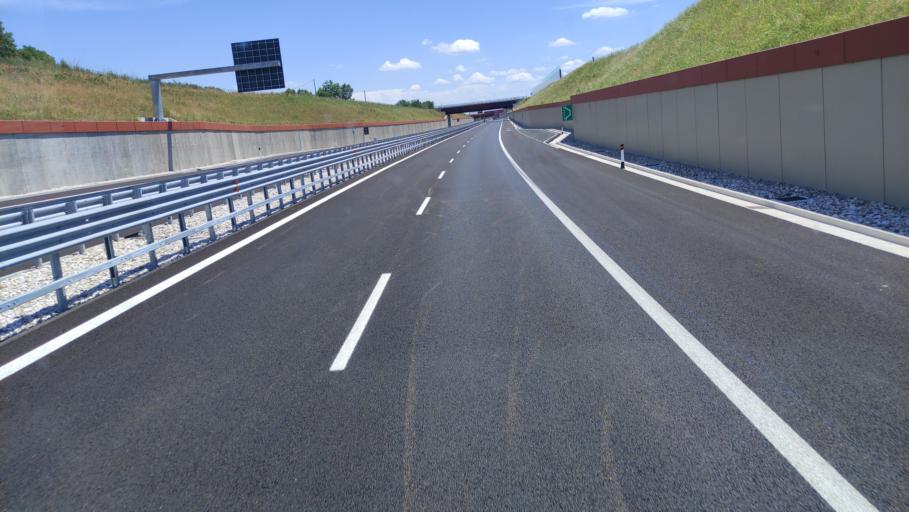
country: IT
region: Veneto
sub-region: Provincia di Treviso
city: Caselle
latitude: 45.7298
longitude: 11.9805
